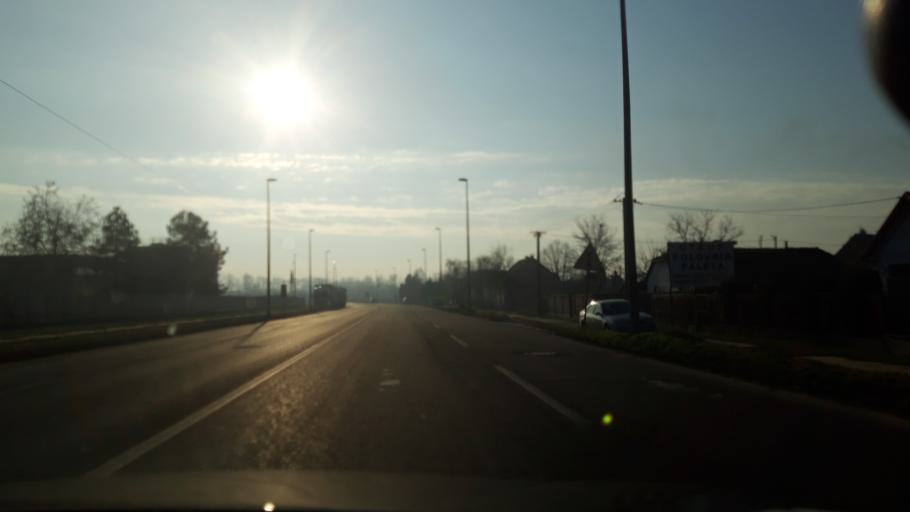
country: RS
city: Pocerski Pricinovic
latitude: 44.7427
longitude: 19.7215
